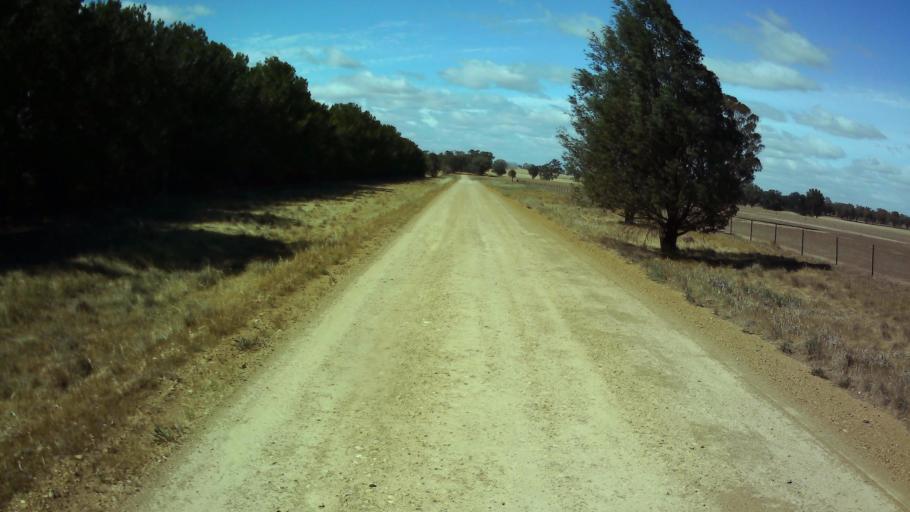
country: AU
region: New South Wales
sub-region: Weddin
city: Grenfell
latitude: -34.0580
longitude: 148.3126
